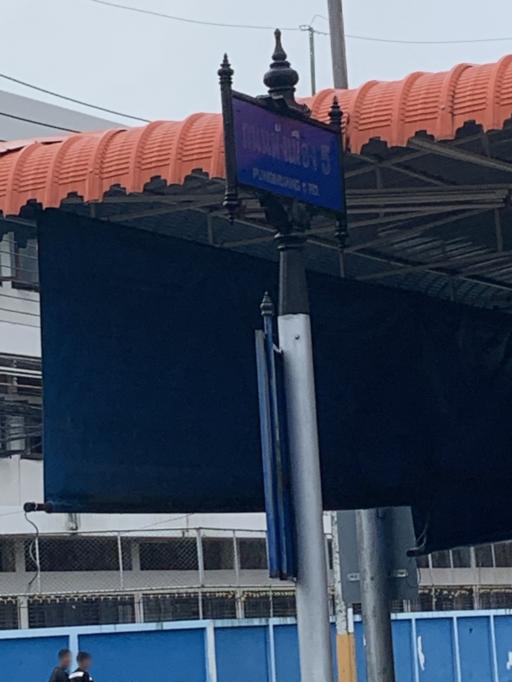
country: TH
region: Yala
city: Yala
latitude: 6.5409
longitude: 101.2855
